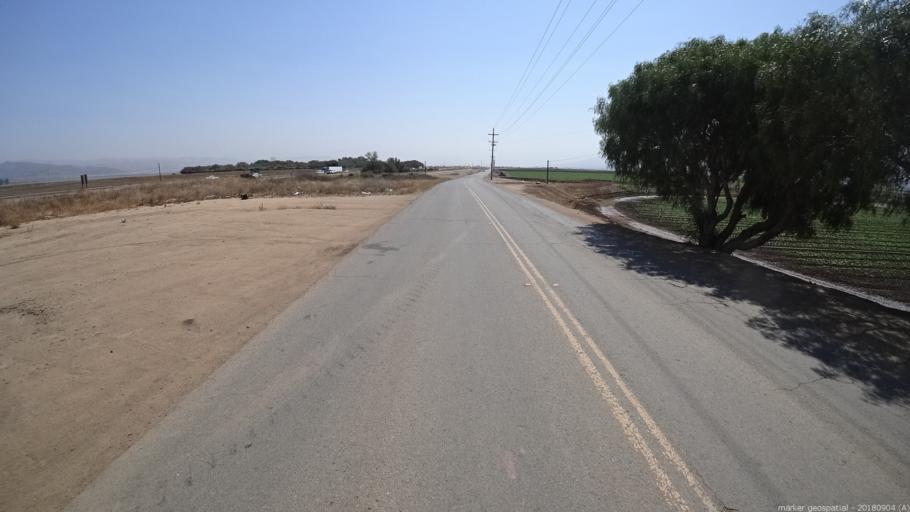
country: US
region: California
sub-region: Monterey County
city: Chualar
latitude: 36.5642
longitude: -121.5142
